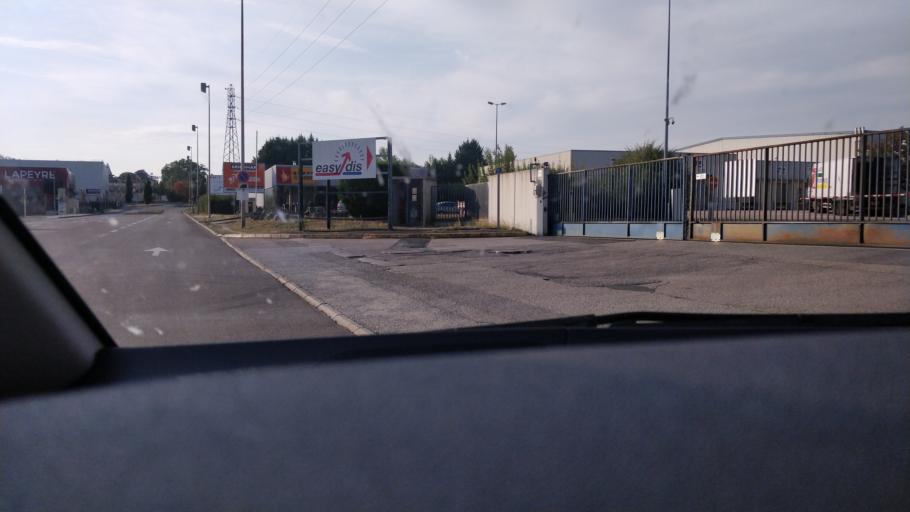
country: FR
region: Limousin
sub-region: Departement de la Haute-Vienne
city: Chaptelat
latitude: 45.8847
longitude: 1.2818
